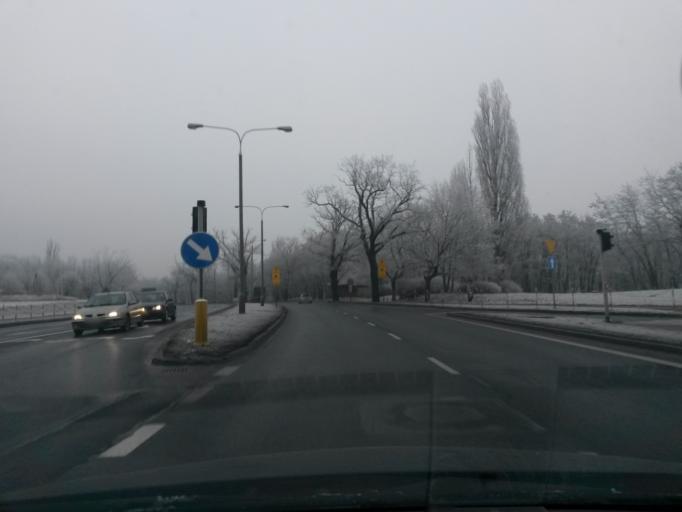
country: PL
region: Greater Poland Voivodeship
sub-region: Powiat gnieznienski
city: Gniezno
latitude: 52.5349
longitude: 17.5828
